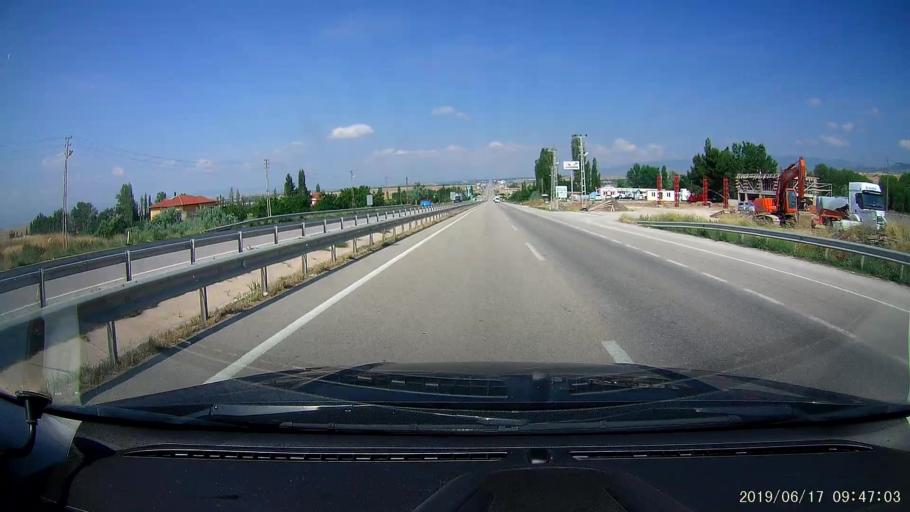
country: TR
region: Amasya
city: Suluova
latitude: 40.8773
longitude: 35.5881
